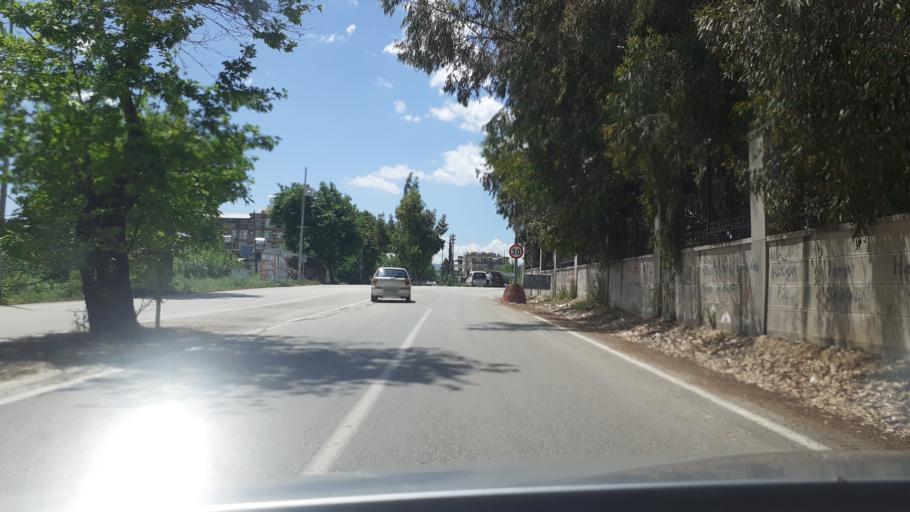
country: TR
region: Hatay
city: Anayazi
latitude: 36.3221
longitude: 36.1978
